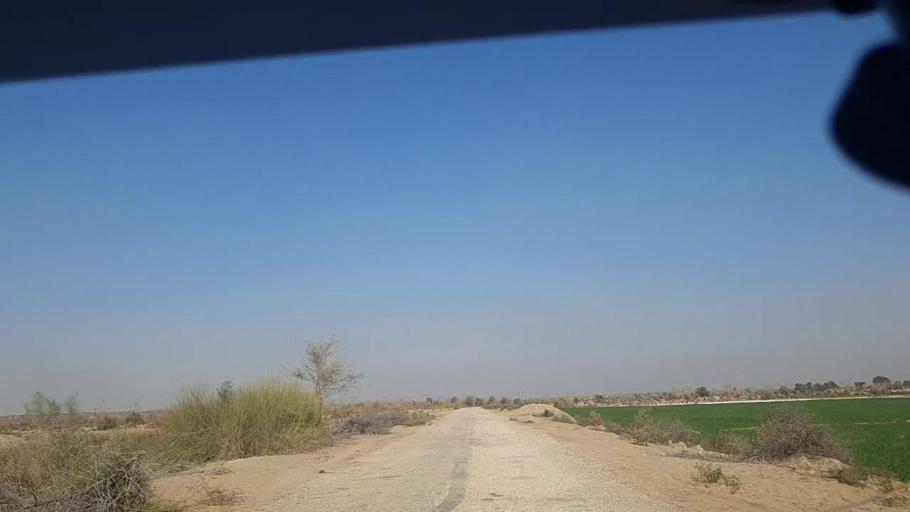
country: PK
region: Sindh
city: Khanpur
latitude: 27.5645
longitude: 69.3382
